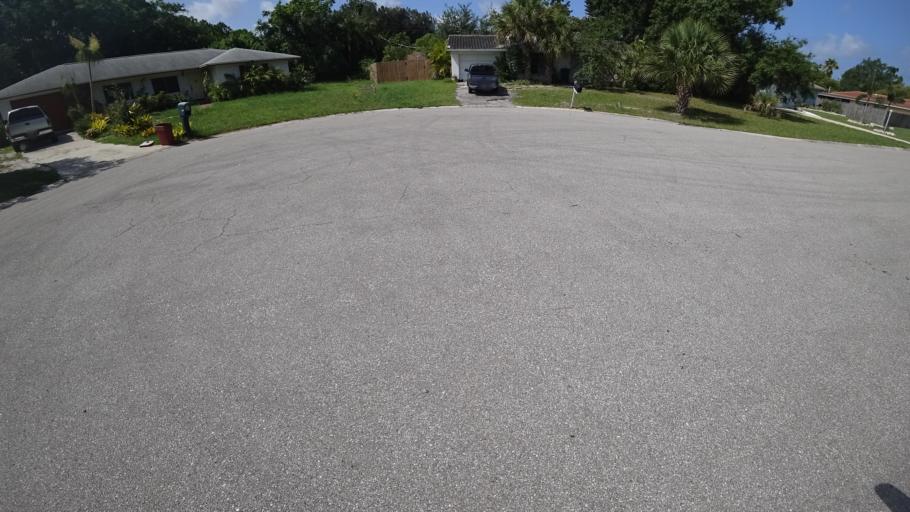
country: US
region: Florida
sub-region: Manatee County
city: Whitfield
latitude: 27.3950
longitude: -82.5652
